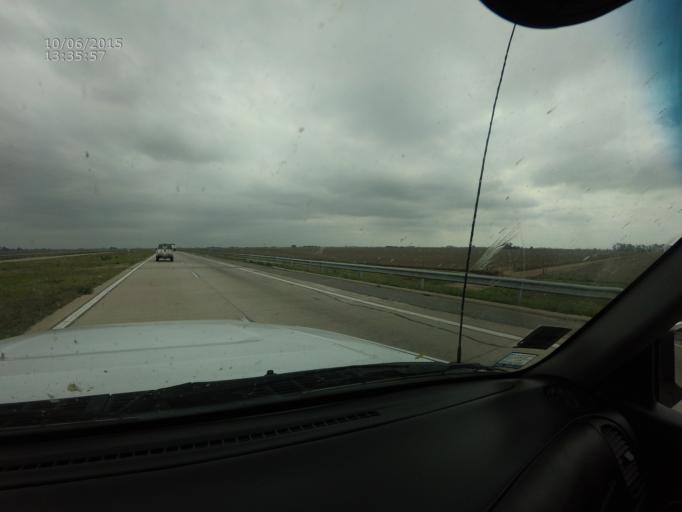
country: AR
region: Cordoba
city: Leones
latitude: -32.6142
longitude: -62.3823
